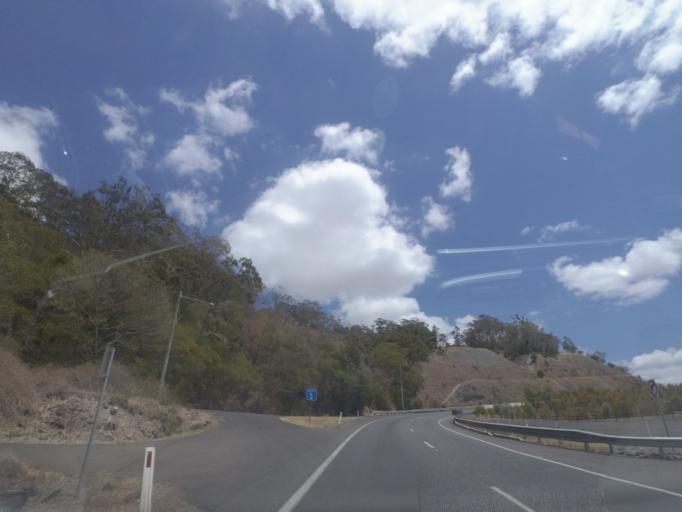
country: AU
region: Queensland
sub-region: Toowoomba
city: East Toowoomba
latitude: -27.5718
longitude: 151.9825
